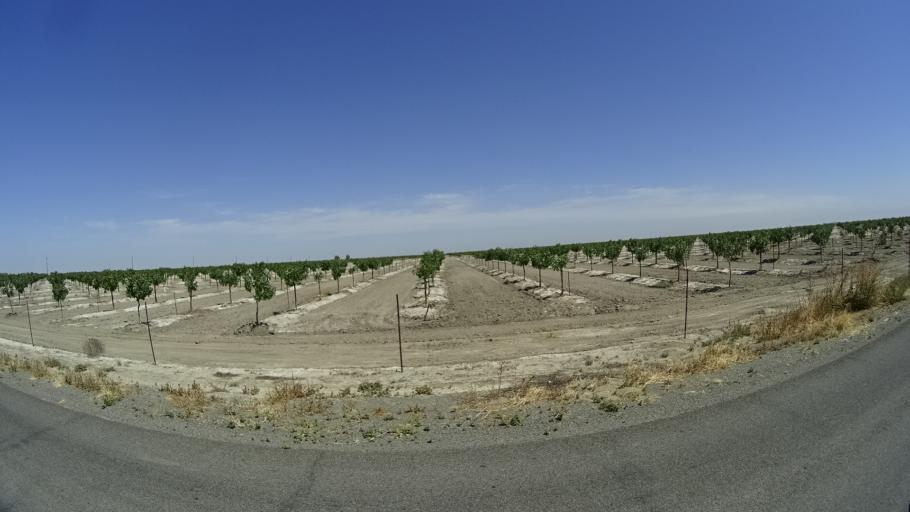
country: US
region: California
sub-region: Kings County
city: Stratford
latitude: 36.1892
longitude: -119.7418
